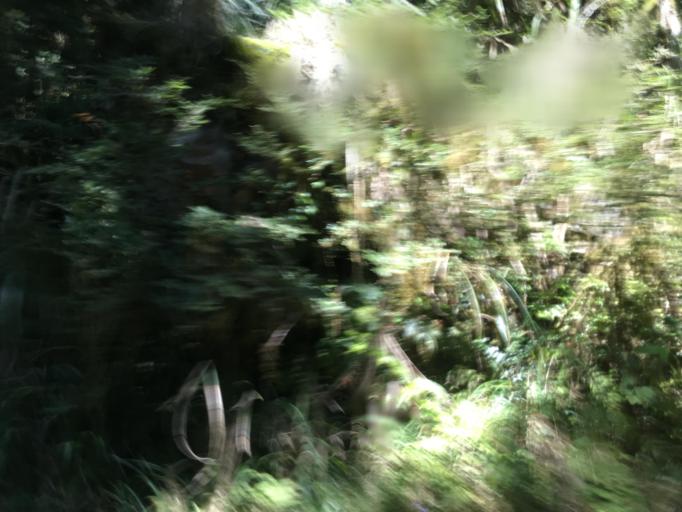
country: TW
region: Taiwan
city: Daxi
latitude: 24.5808
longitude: 121.4114
